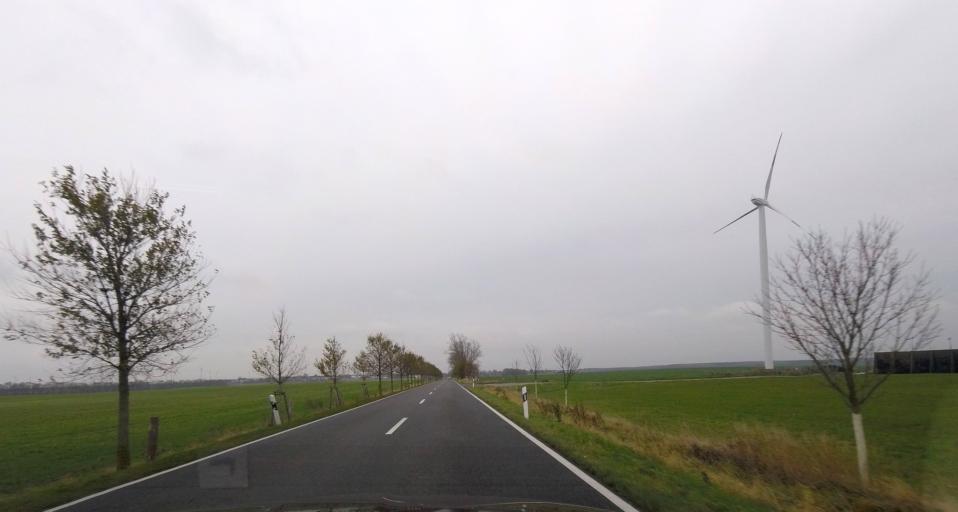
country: DE
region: Saxony-Anhalt
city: Kropstadt
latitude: 52.0110
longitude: 12.7609
